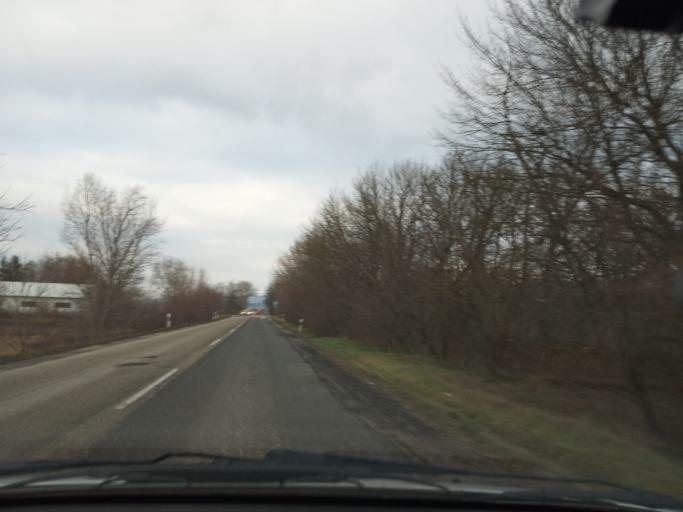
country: HU
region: Komarom-Esztergom
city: Esztergom
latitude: 47.7604
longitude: 18.7358
